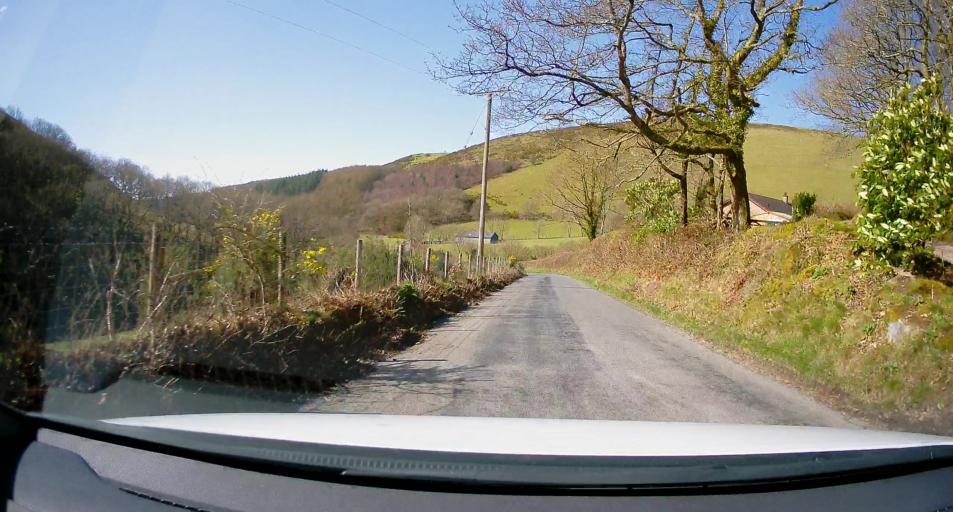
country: GB
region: Wales
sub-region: County of Ceredigion
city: Lledrod
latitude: 52.3535
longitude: -3.9159
